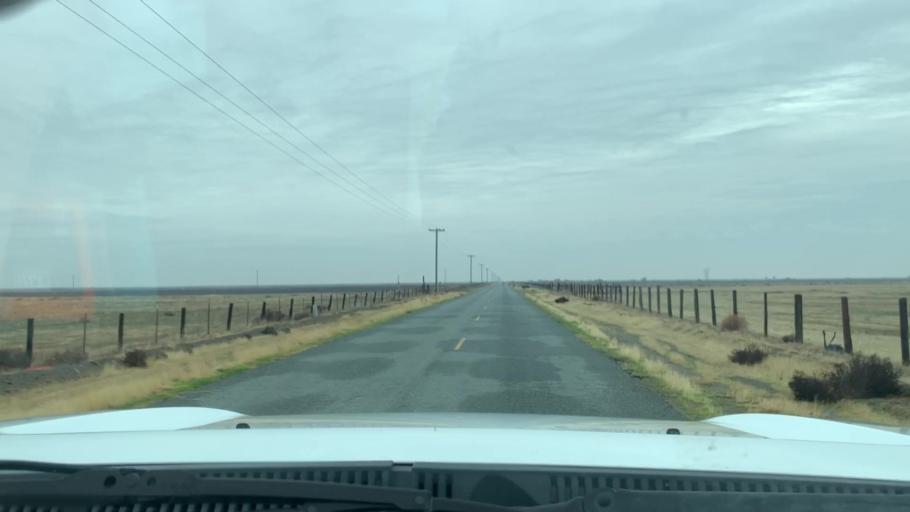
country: US
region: California
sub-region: Tulare County
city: Alpaugh
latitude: 35.7609
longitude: -119.5494
